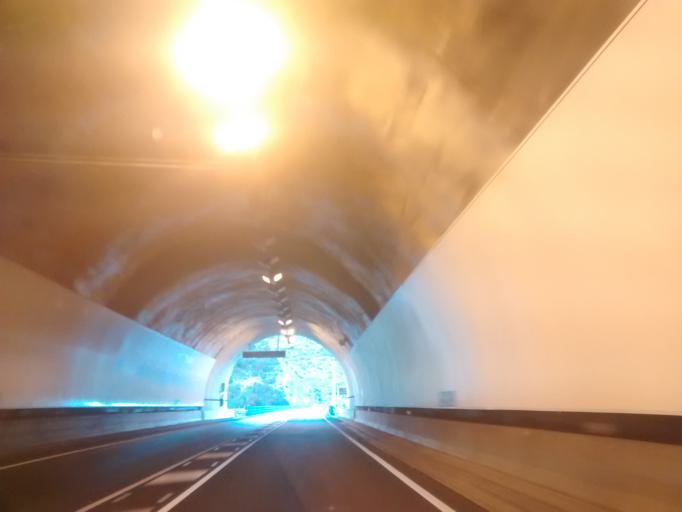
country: ES
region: Catalonia
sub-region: Provincia de Lleida
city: Coll de Nargo
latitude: 42.1471
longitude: 1.3067
